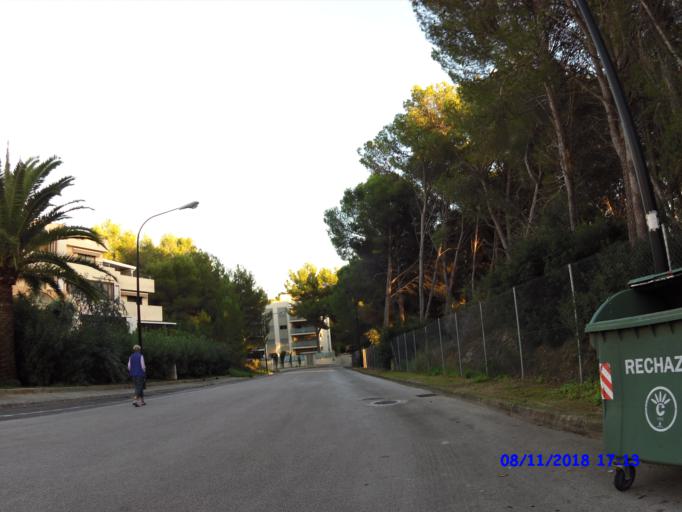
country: ES
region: Balearic Islands
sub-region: Illes Balears
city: Santa Ponsa
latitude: 39.5331
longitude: 2.4631
